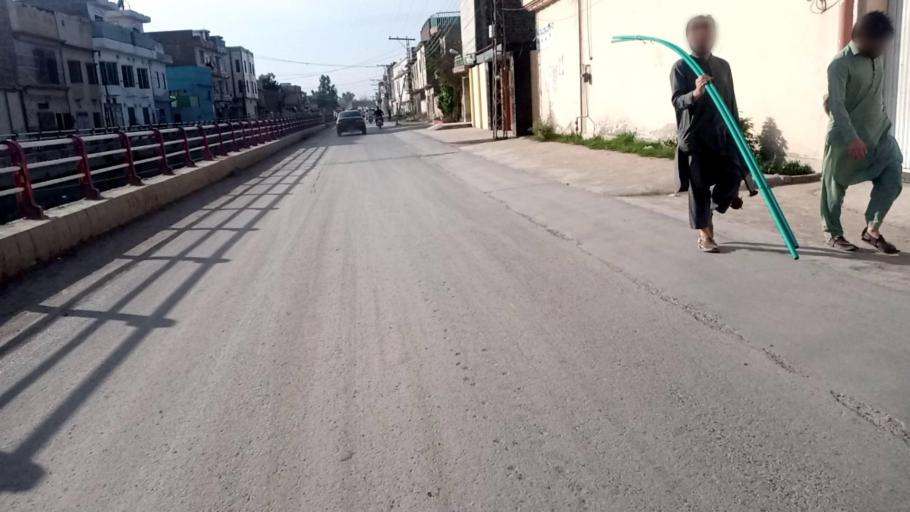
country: PK
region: Khyber Pakhtunkhwa
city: Peshawar
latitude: 34.0136
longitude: 71.6099
